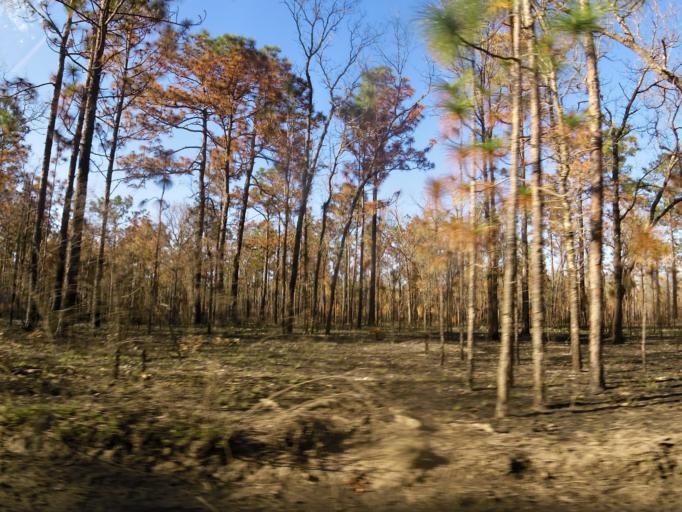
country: US
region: Florida
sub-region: Clay County
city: Middleburg
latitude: 30.1302
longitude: -81.8955
